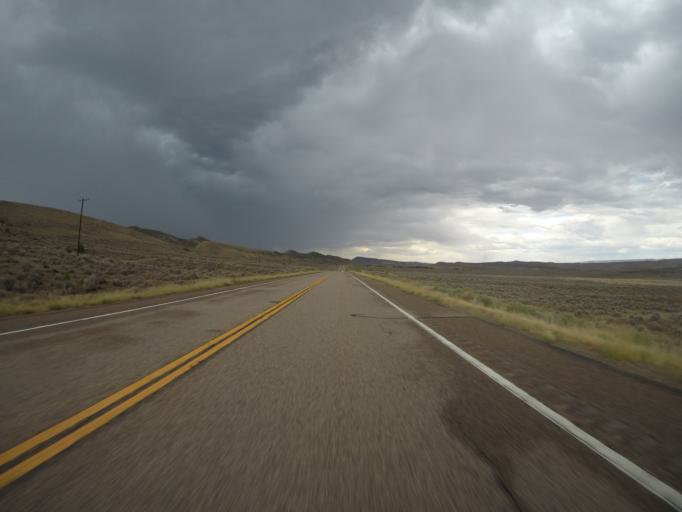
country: US
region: Colorado
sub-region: Rio Blanco County
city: Rangely
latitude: 40.2449
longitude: -108.8853
